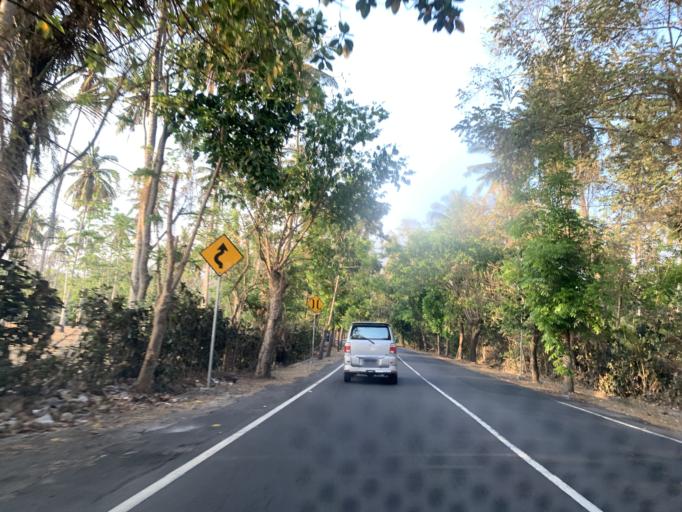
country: ID
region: Bali
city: Angkahgede
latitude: -8.4843
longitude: 114.9443
